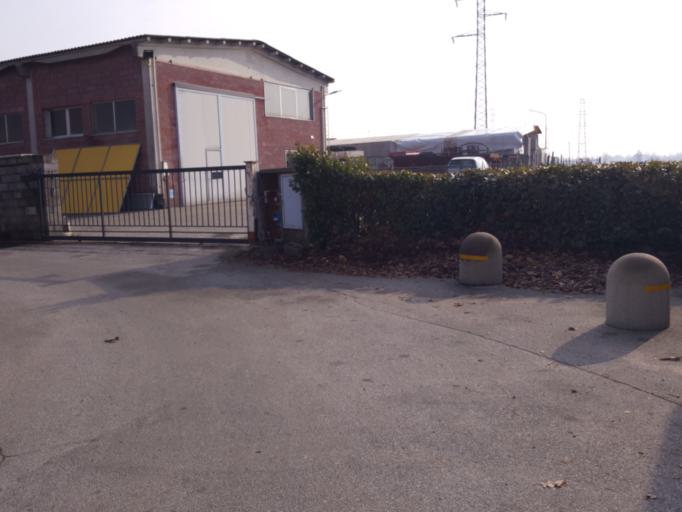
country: IT
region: Piedmont
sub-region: Provincia di Novara
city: Cressa
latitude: 45.6458
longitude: 8.5057
